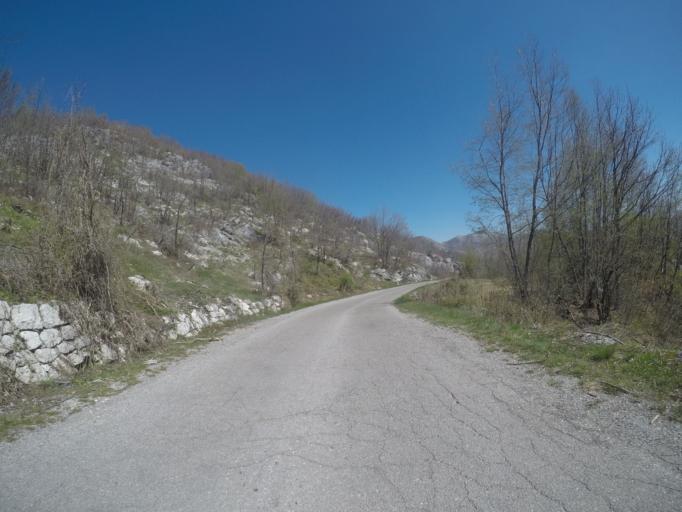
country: ME
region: Cetinje
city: Cetinje
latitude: 42.4362
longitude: 18.8693
